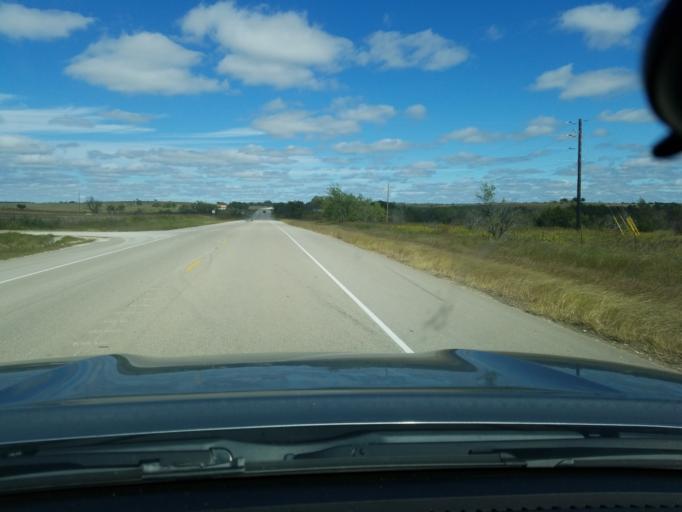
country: US
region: Texas
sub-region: Hamilton County
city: Hamilton
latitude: 31.6402
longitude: -98.1497
